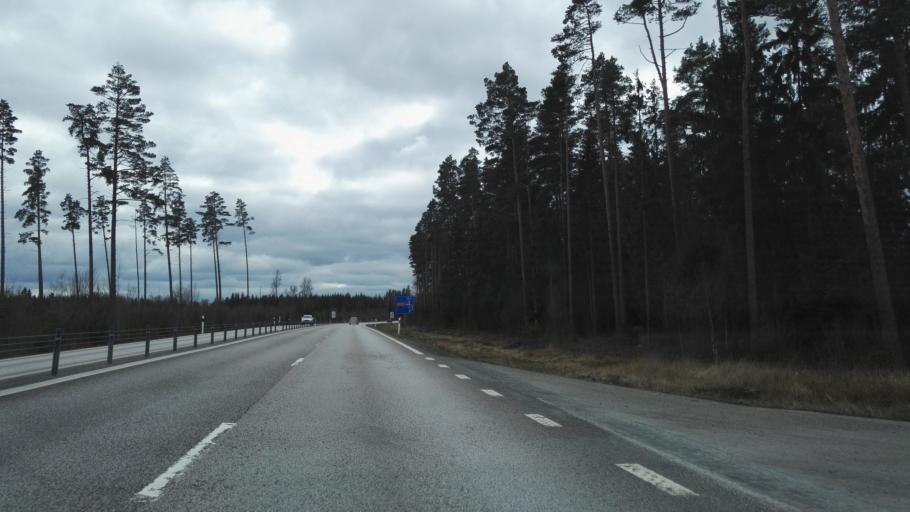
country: SE
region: Kronoberg
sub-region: Alvesta Kommun
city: Vislanda
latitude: 56.7574
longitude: 14.5223
